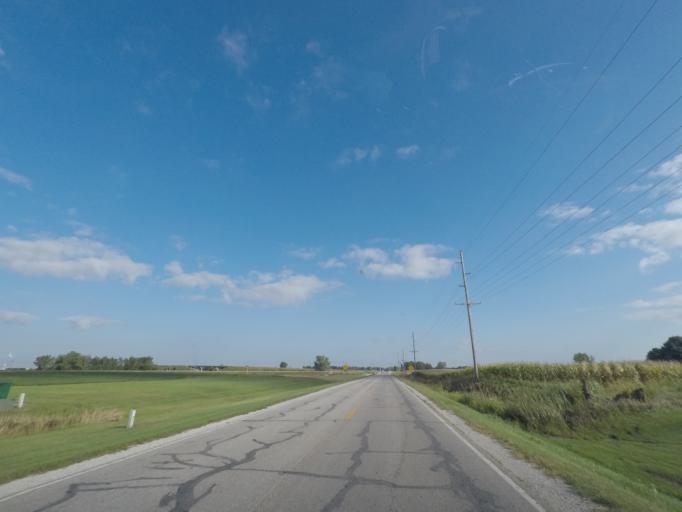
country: US
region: Iowa
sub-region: Story County
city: Nevada
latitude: 42.0022
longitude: -93.4628
